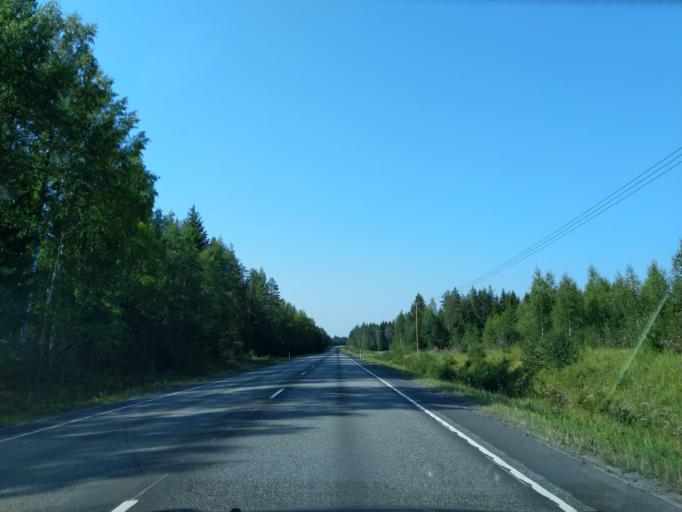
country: FI
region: Satakunta
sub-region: Pori
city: Pomarkku
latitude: 61.7177
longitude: 22.0483
